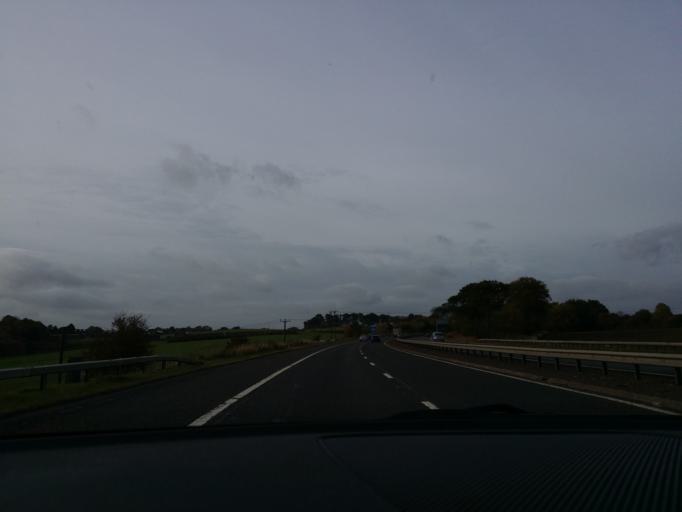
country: GB
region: Scotland
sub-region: Edinburgh
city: Kirkliston
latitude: 55.9584
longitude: -3.4361
